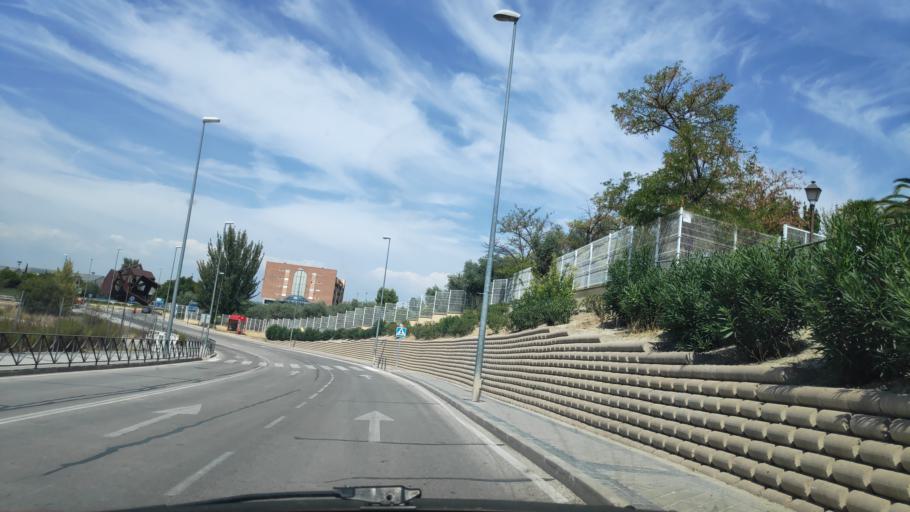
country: ES
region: Madrid
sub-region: Provincia de Madrid
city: Arganda
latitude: 40.3053
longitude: -3.4457
